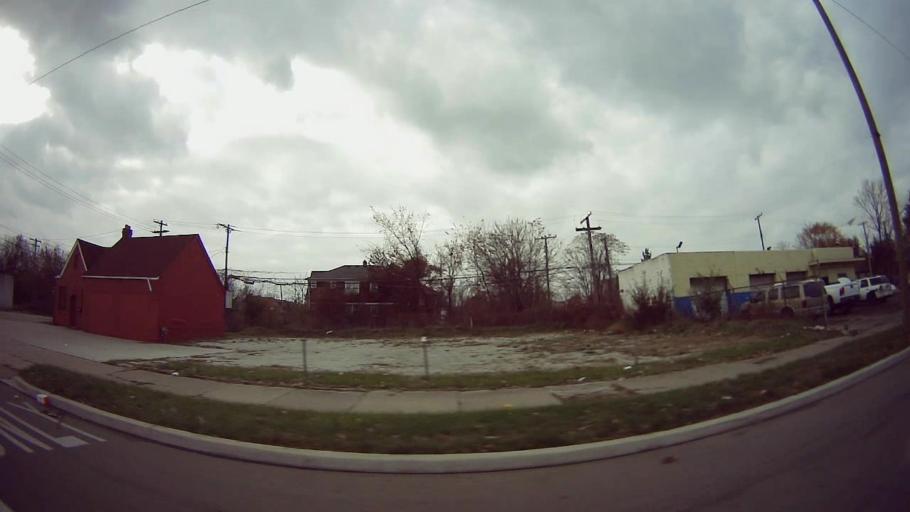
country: US
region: Michigan
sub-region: Wayne County
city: Highland Park
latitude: 42.4008
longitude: -83.1403
